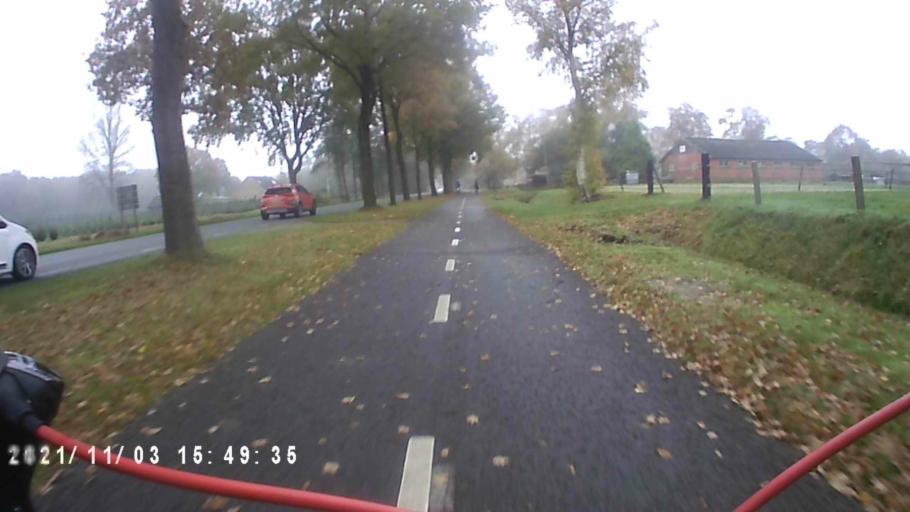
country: NL
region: Groningen
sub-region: Gemeente Leek
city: Leek
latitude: 53.0837
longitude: 6.3377
